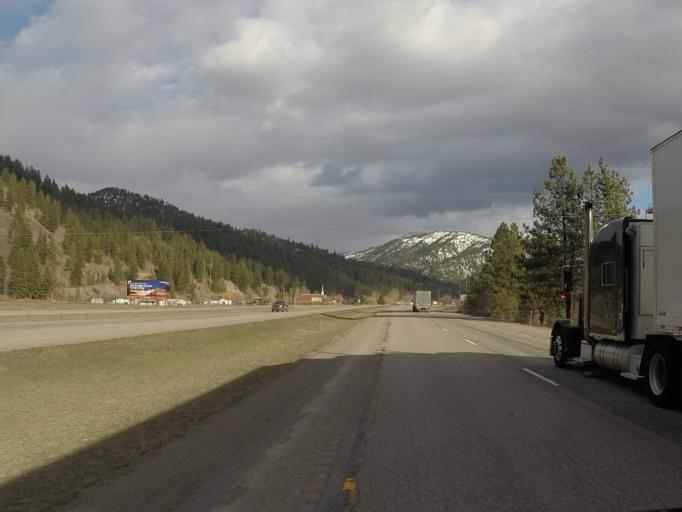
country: US
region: Montana
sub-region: Missoula County
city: Clinton
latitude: 46.7890
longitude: -113.7273
